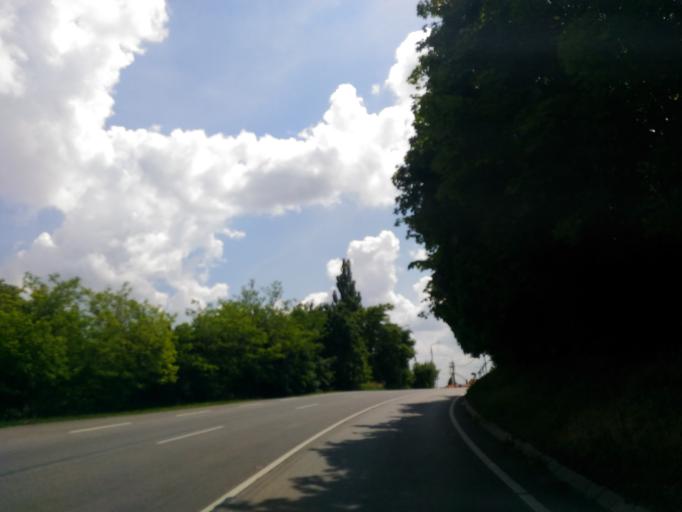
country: HU
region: Baranya
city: Pecs
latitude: 46.1220
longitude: 18.2615
